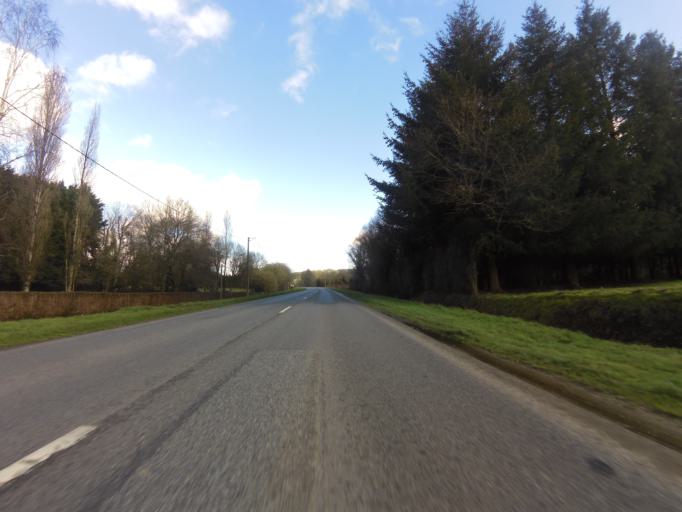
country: FR
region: Brittany
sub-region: Departement du Morbihan
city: Guern
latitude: 48.0761
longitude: -3.1169
